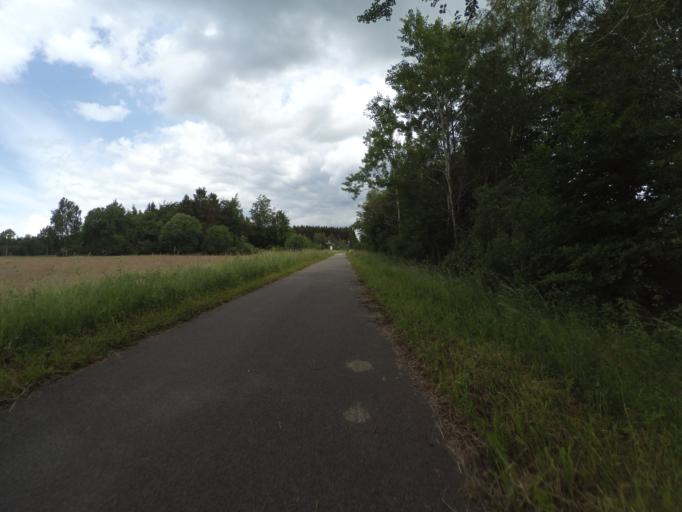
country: DE
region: North Rhine-Westphalia
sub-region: Regierungsbezirk Koln
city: Monschau
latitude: 50.5895
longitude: 6.2421
